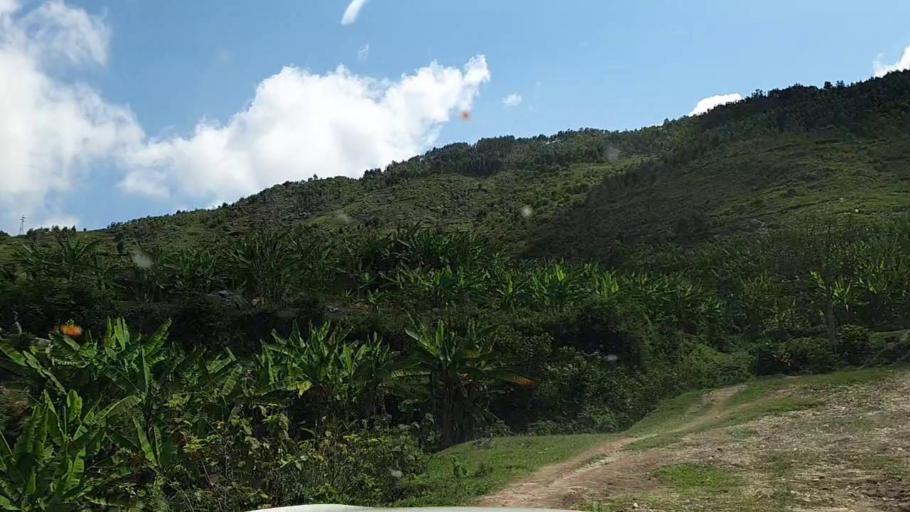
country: RW
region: Southern Province
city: Gikongoro
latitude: -2.3625
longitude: 29.5318
